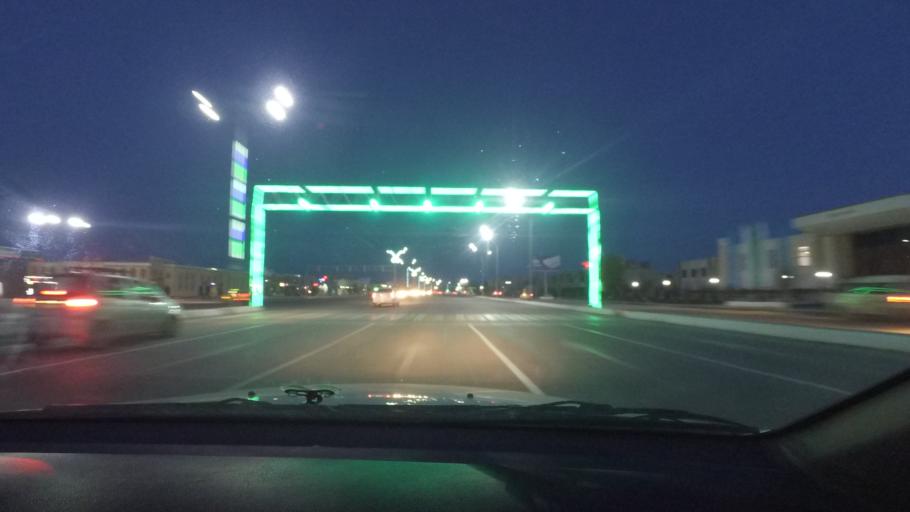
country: UZ
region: Bukhara
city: Bukhara
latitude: 39.7836
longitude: 64.4200
